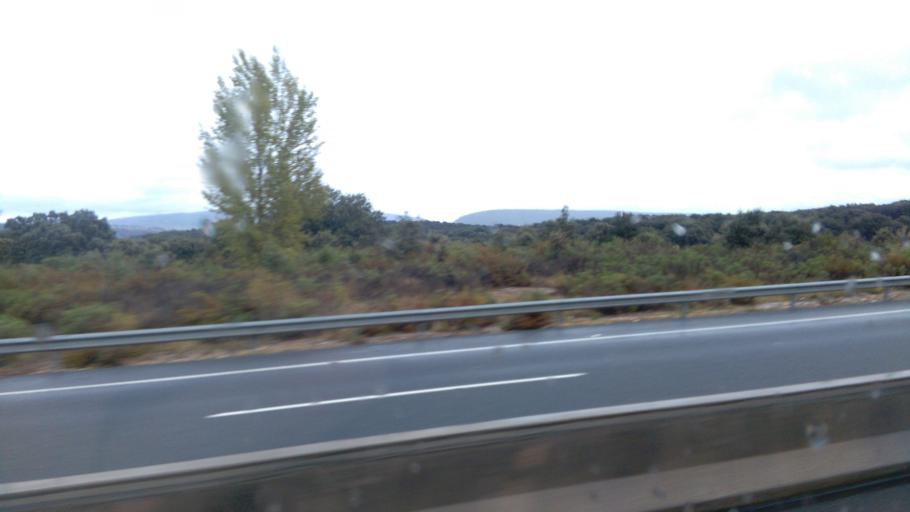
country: ES
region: Extremadura
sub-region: Provincia de Caceres
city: Casas de Miravete
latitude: 39.7683
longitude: -5.7364
